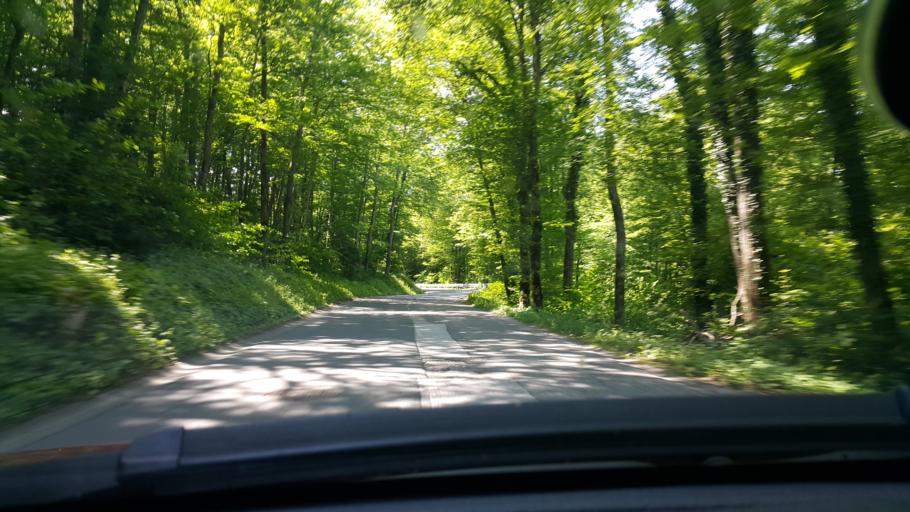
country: SI
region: Novo Mesto
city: Novo Mesto
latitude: 45.7629
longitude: 15.1702
